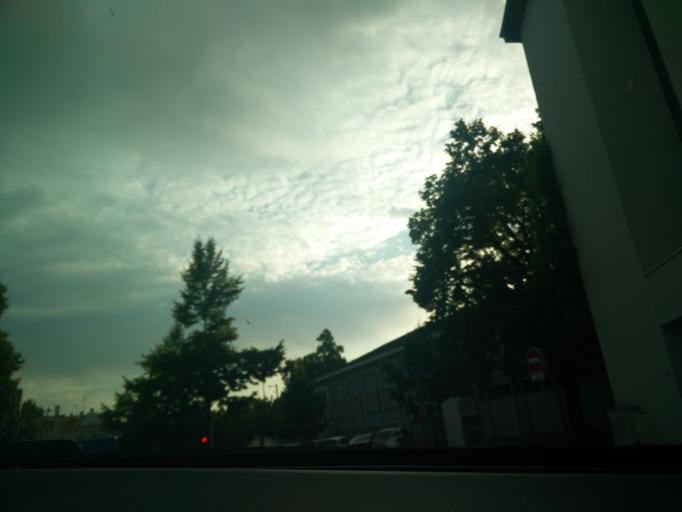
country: FR
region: Alsace
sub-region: Departement du Bas-Rhin
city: Strasbourg
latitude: 48.5675
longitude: 7.7678
